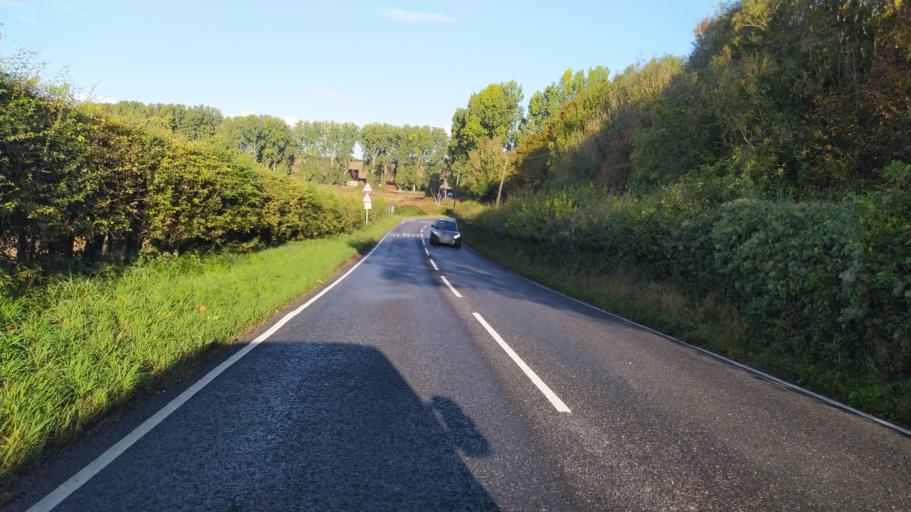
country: GB
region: England
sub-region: Dorset
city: Wimborne Minster
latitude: 50.8784
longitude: -1.9801
